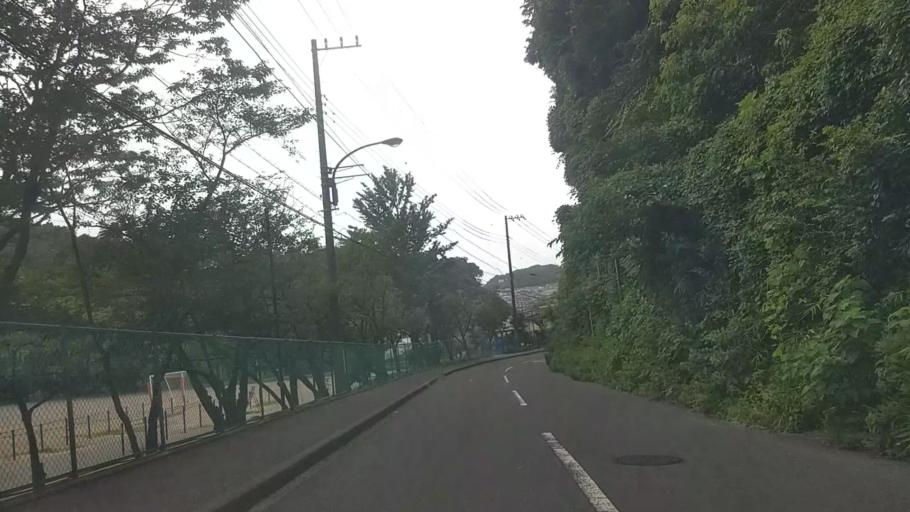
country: JP
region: Kanagawa
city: Yokosuka
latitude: 35.2520
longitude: 139.7323
